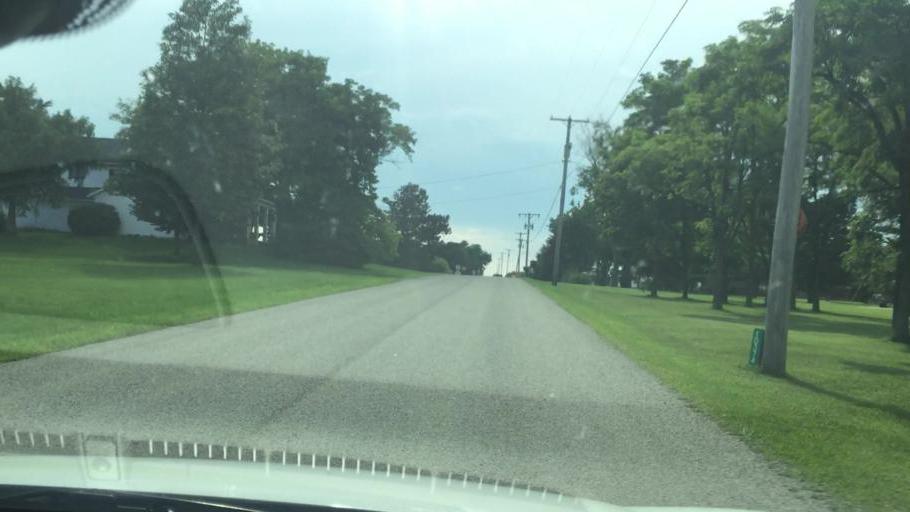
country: US
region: Ohio
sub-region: Clark County
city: Lisbon
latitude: 39.9451
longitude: -83.6089
